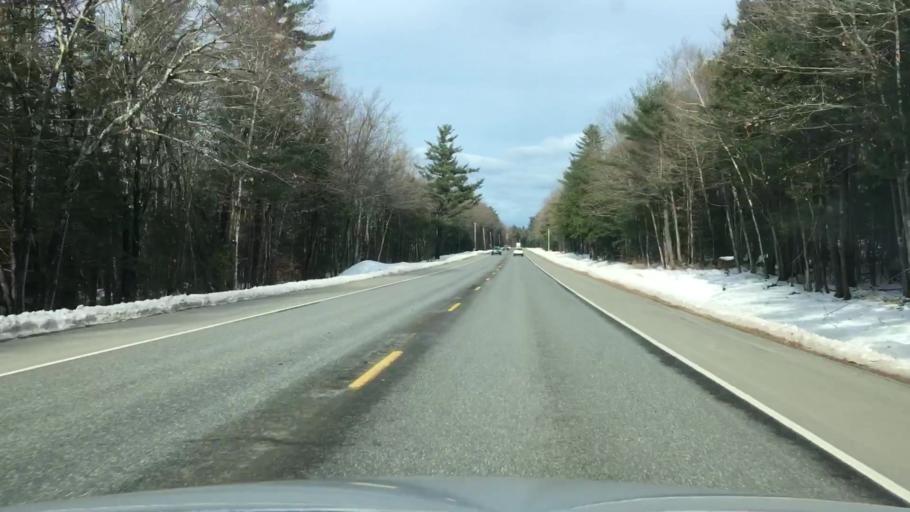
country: US
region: Maine
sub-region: Kennebec County
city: Monmouth
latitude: 44.2412
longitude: -70.0681
